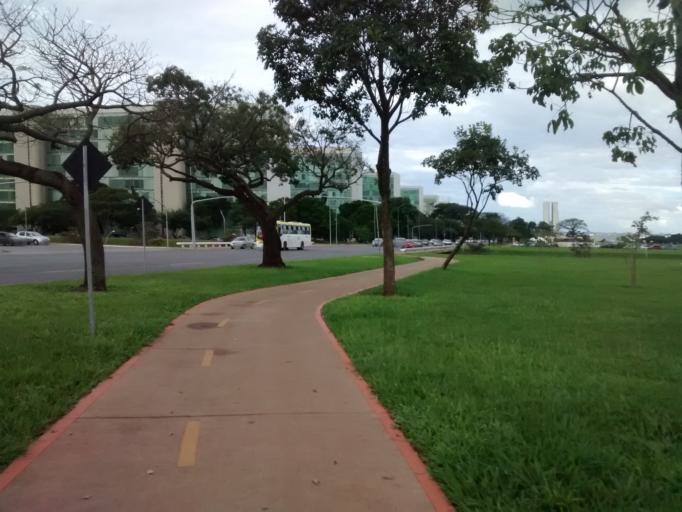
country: BR
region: Federal District
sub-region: Brasilia
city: Brasilia
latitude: -15.7950
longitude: -47.8767
